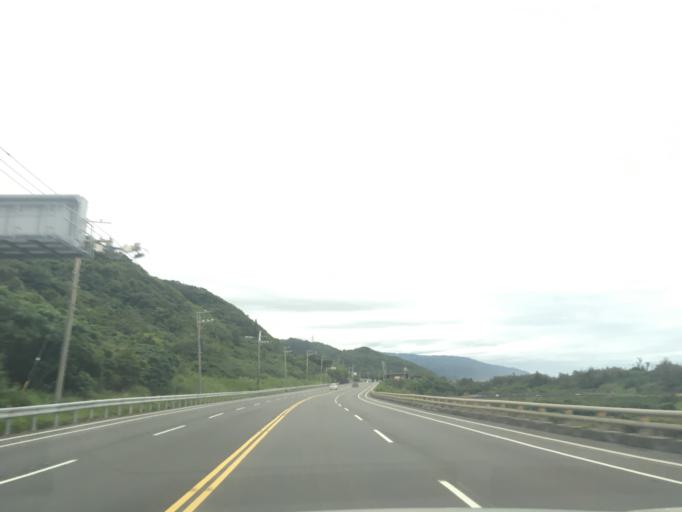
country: TW
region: Taiwan
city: Hengchun
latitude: 22.2985
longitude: 120.8888
